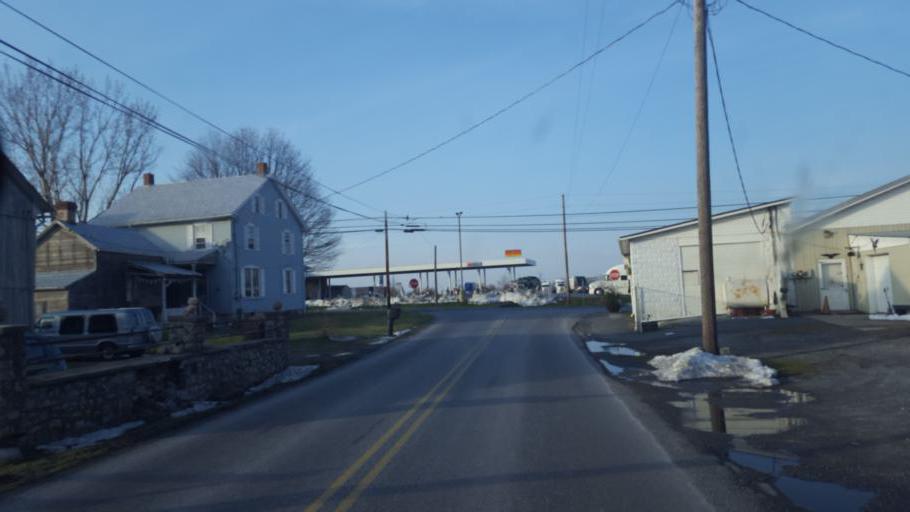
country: US
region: Pennsylvania
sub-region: Lancaster County
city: East Earl
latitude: 40.1131
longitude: -76.0315
